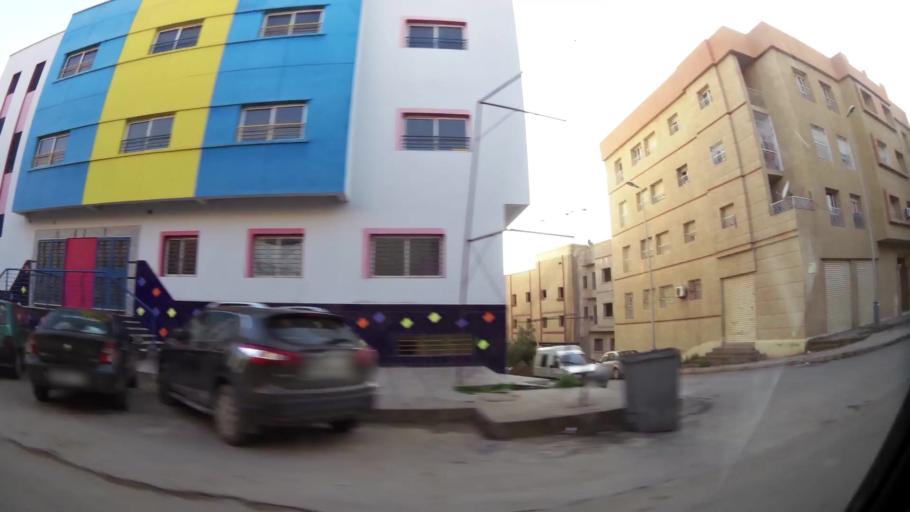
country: MA
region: Chaouia-Ouardigha
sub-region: Settat Province
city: Settat
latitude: 32.9881
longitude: -7.6095
